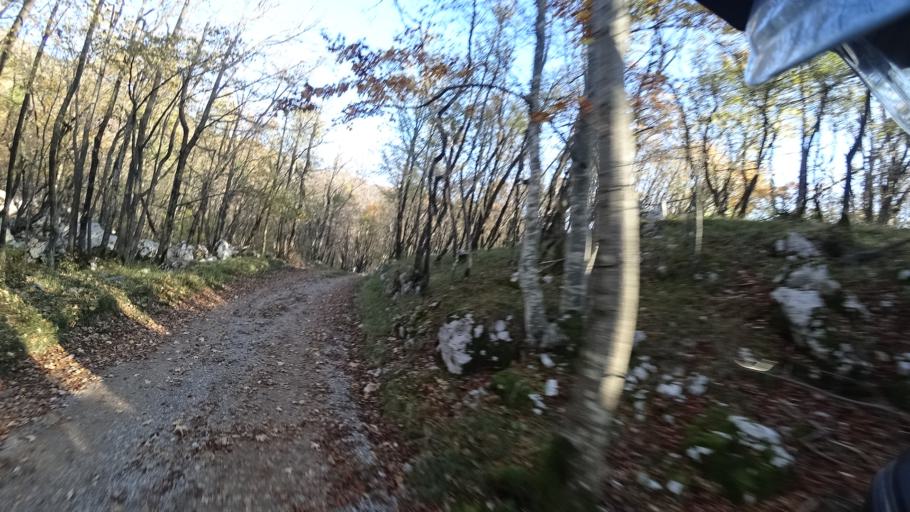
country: HR
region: Primorsko-Goranska
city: Klana
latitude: 45.4837
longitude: 14.4206
